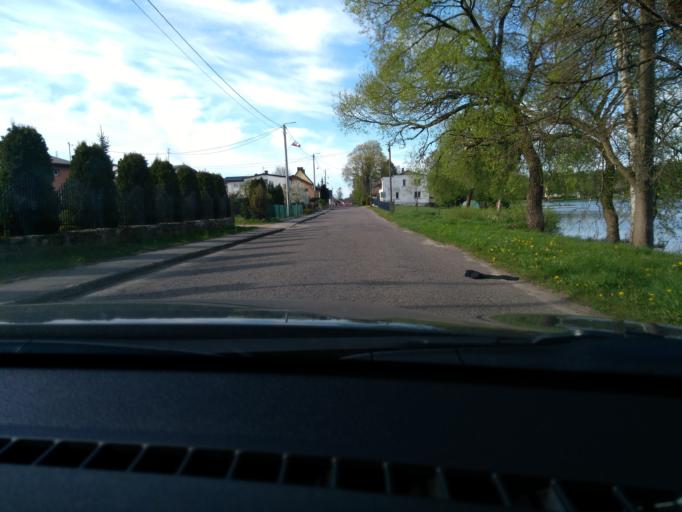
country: PL
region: Pomeranian Voivodeship
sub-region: Powiat leborski
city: Cewice
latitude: 54.3333
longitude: 17.6848
